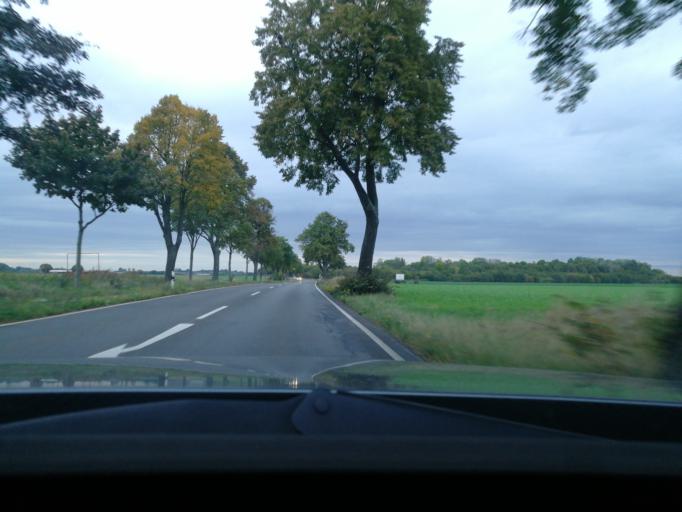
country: DE
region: North Rhine-Westphalia
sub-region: Regierungsbezirk Dusseldorf
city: Dormagen
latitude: 51.1207
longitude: 6.7666
